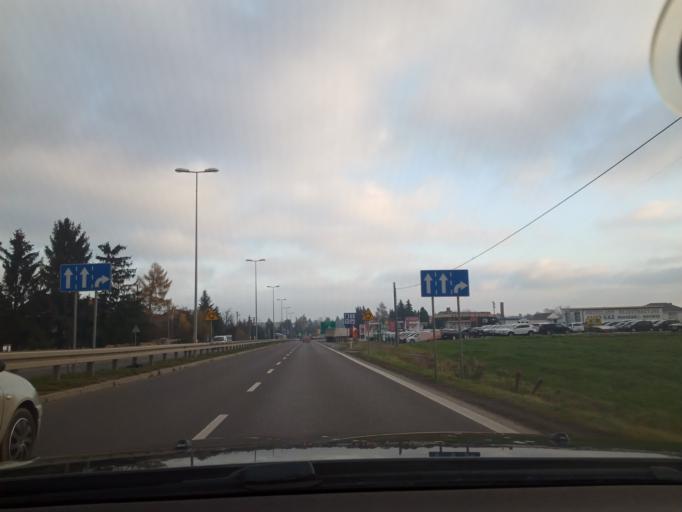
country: PL
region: Lesser Poland Voivodeship
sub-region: Powiat wielicki
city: Wegrzce Wielkie
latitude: 50.1244
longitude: 20.0999
